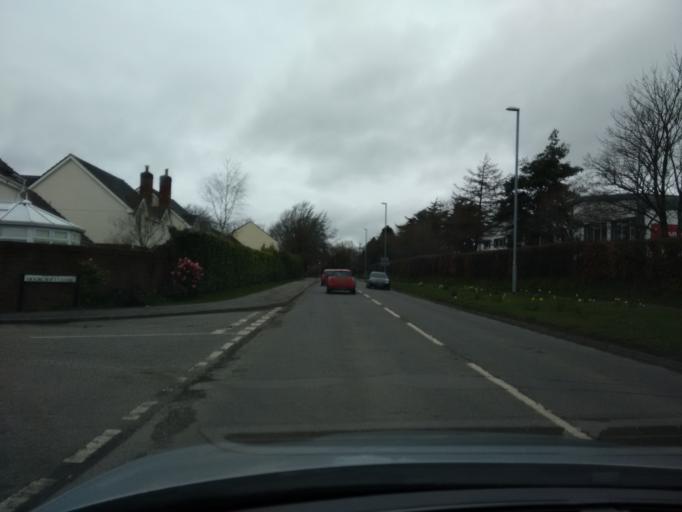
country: GB
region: England
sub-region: Devon
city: Okehampton
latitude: 50.7412
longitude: -3.9818
